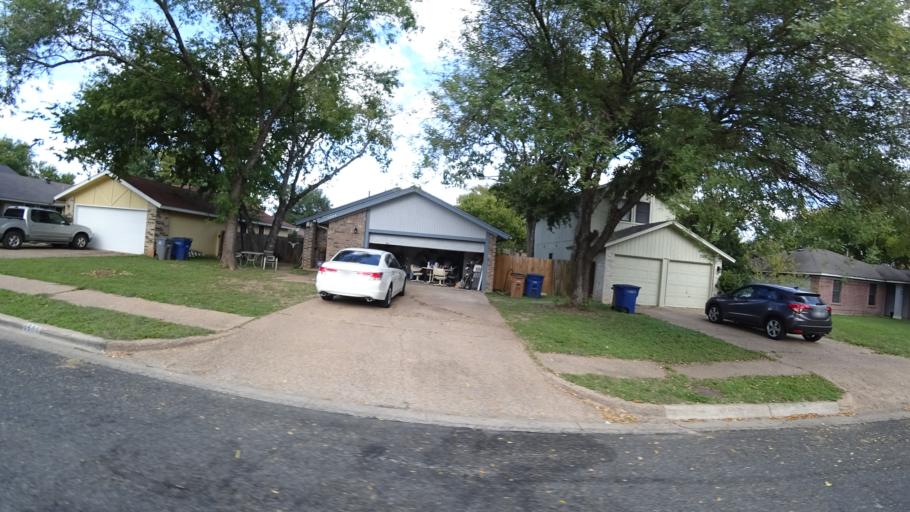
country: US
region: Texas
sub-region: Travis County
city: Onion Creek
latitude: 30.1929
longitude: -97.7354
